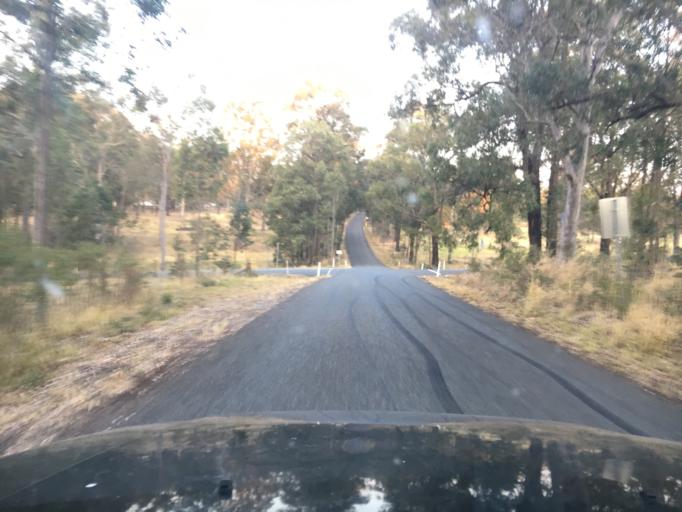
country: AU
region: New South Wales
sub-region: Cessnock
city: Branxton
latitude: -32.6316
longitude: 151.3661
